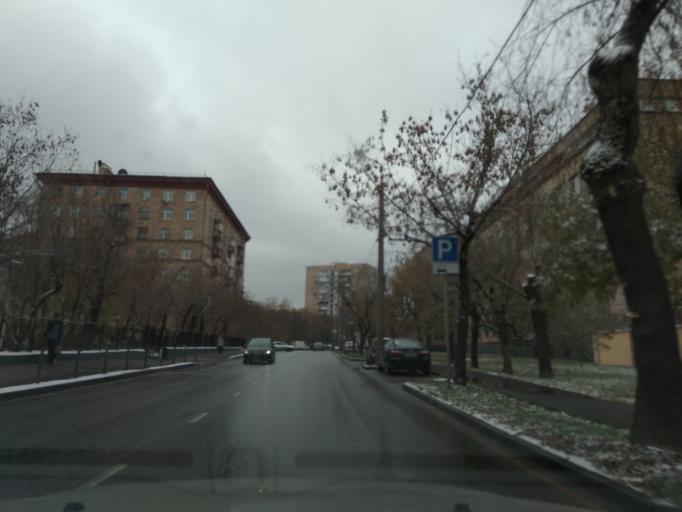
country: RU
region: Moscow
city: Pokrovskoye-Streshnevo
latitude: 55.8014
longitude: 37.4733
